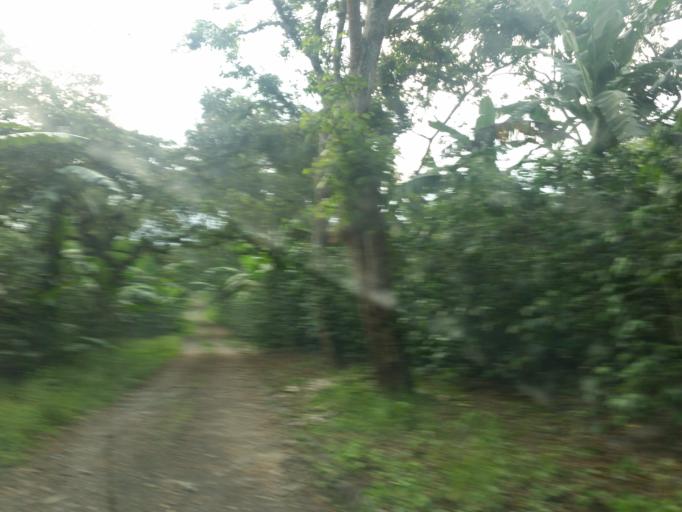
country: MX
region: Veracruz
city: Coatepec
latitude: 19.4282
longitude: -96.9576
